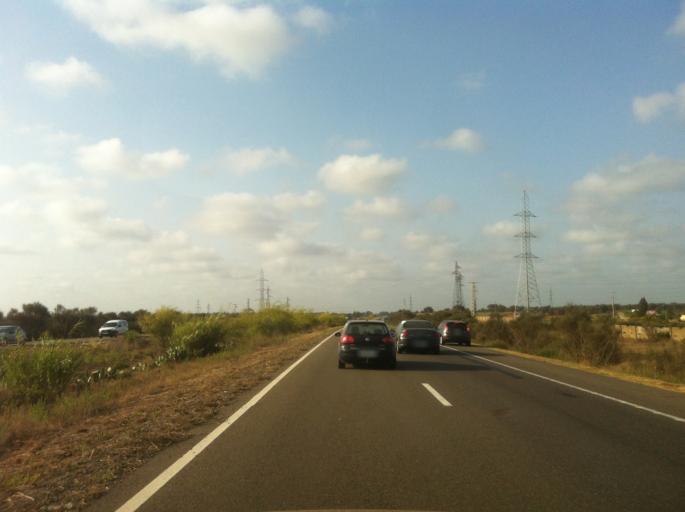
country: MA
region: Gharb-Chrarda-Beni Hssen
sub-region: Kenitra Province
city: Kenitra
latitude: 34.2283
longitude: -6.5578
